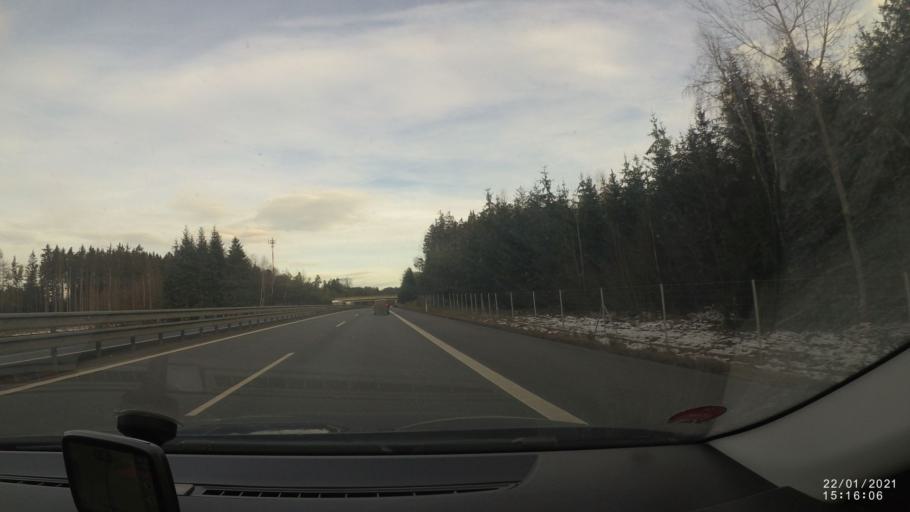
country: CZ
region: Plzensky
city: Holoubkov
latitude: 49.7801
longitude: 13.6854
